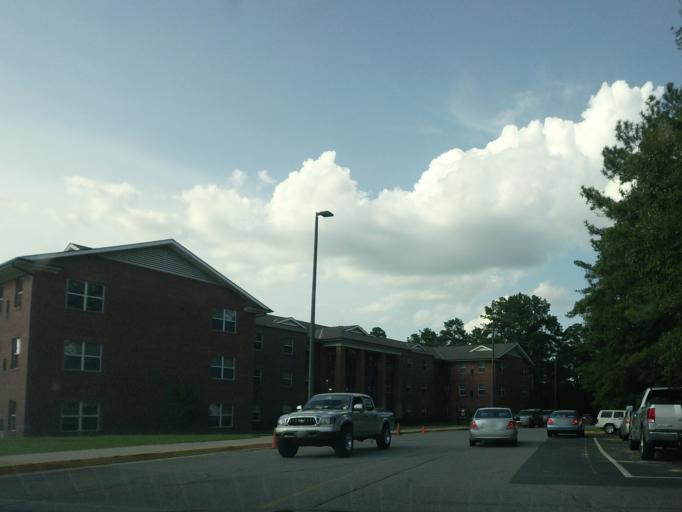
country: US
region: Georgia
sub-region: Bleckley County
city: Cochran
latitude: 32.3812
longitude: -83.3406
